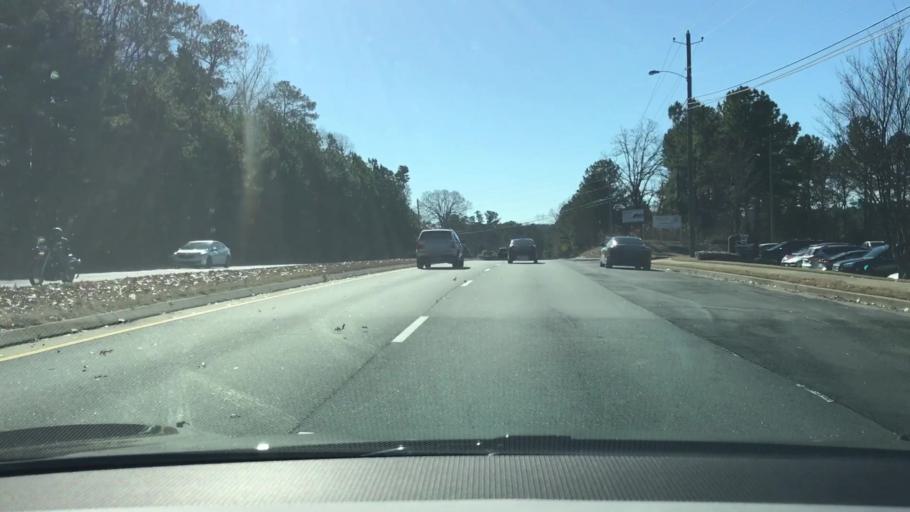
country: US
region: Georgia
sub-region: Gwinnett County
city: Suwanee
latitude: 34.0182
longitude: -84.0410
